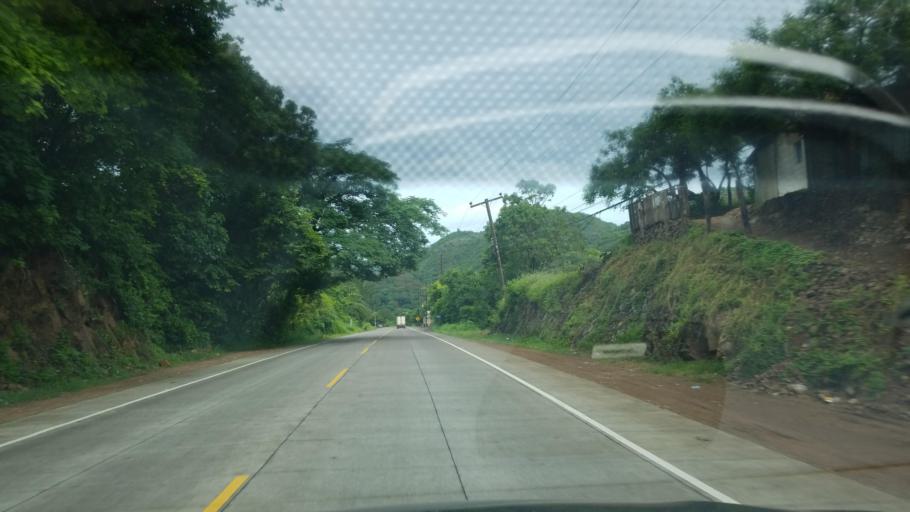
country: HN
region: Francisco Morazan
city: El Porvenir
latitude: 13.6862
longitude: -87.3412
